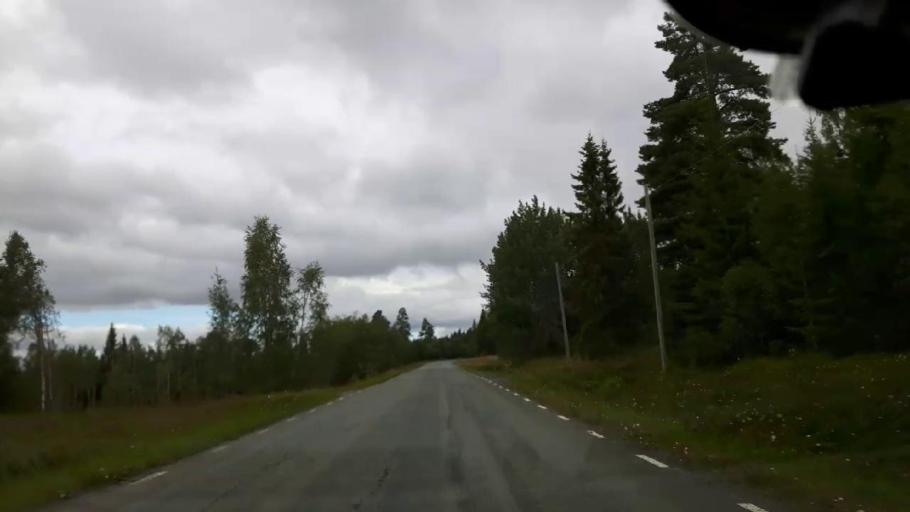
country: SE
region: Jaemtland
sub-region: Krokoms Kommun
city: Valla
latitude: 63.5195
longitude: 13.8742
